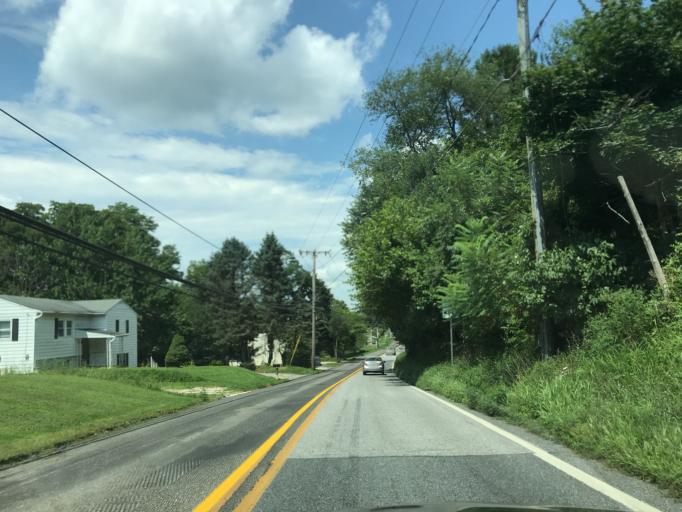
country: US
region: Pennsylvania
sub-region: York County
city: New Freedom
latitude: 39.6684
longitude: -76.7133
